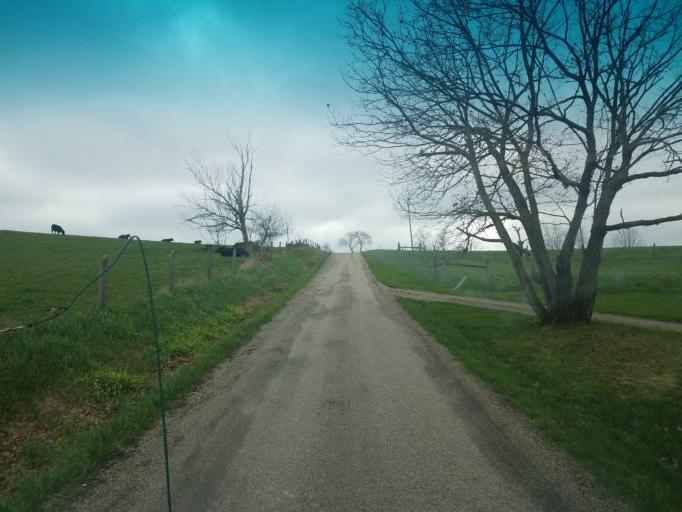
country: US
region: Ohio
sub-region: Stark County
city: Beach City
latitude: 40.6127
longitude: -81.6016
